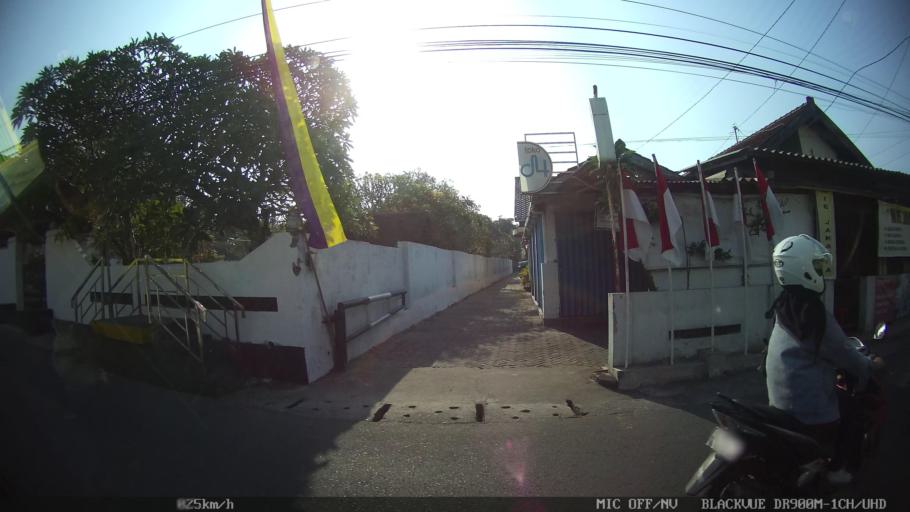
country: ID
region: Daerah Istimewa Yogyakarta
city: Depok
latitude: -7.7787
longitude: 110.4086
